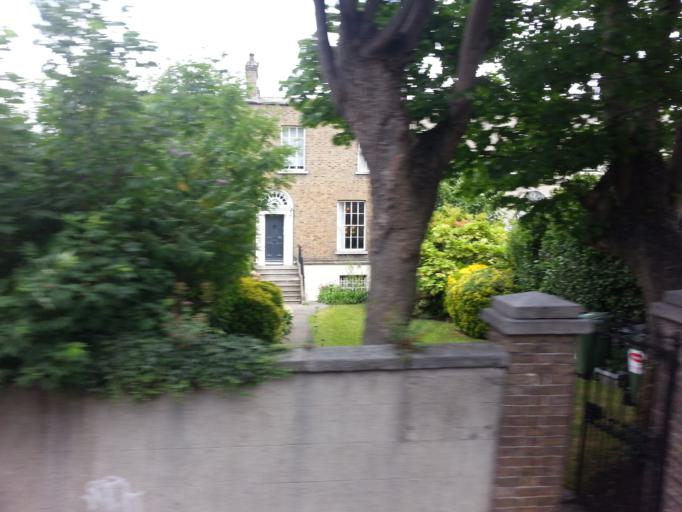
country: IE
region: Leinster
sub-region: Dublin City
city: Dublin
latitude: 53.3238
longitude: -6.2511
